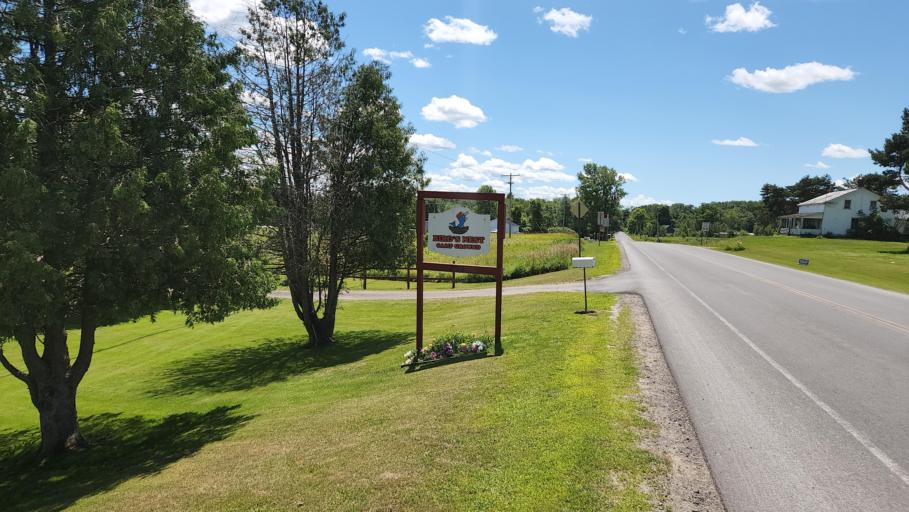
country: CA
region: Ontario
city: Brockville
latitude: 44.5099
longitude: -75.6161
